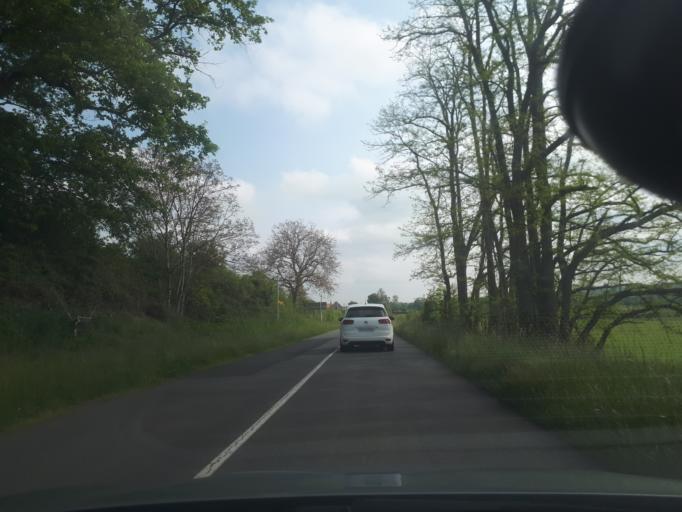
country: FR
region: Auvergne
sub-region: Departement de l'Allier
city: Lapalisse
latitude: 46.3946
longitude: 3.5942
